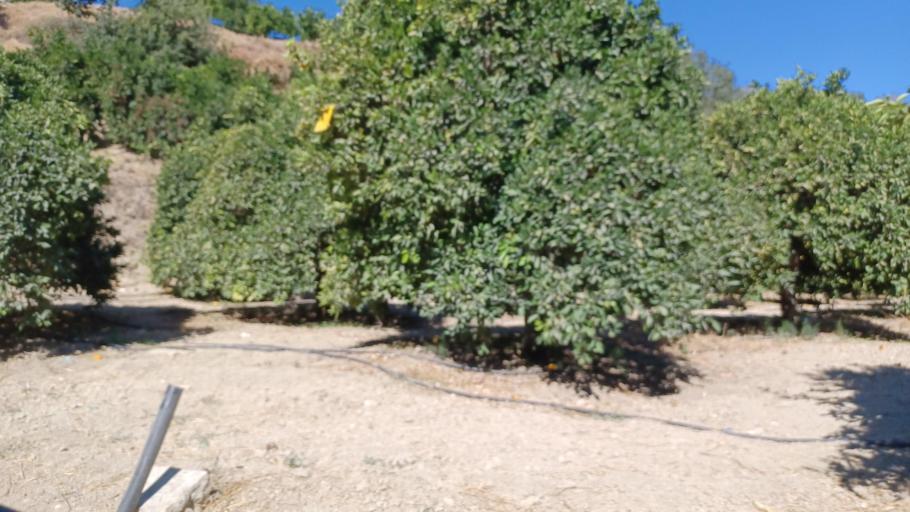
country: CY
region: Pafos
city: Polis
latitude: 34.9442
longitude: 32.4682
